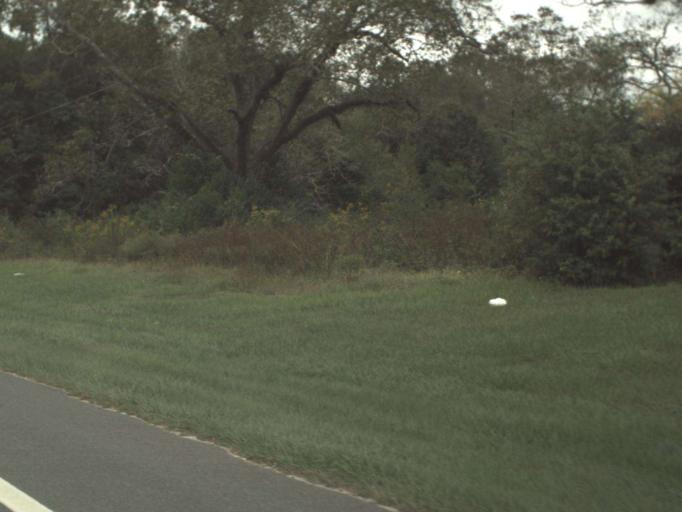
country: US
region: Florida
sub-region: Jackson County
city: Malone
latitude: 30.8700
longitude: -85.1474
